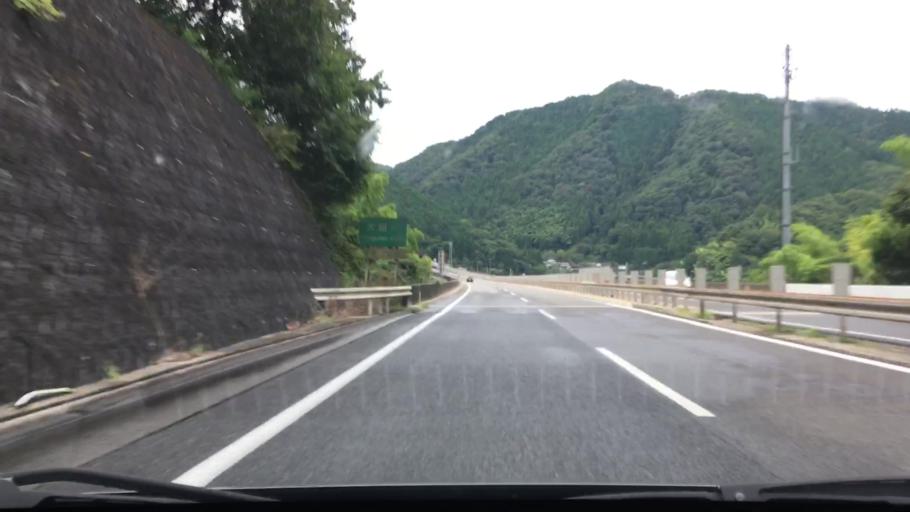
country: JP
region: Hiroshima
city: Hiroshima-shi
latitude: 34.5320
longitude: 132.4380
